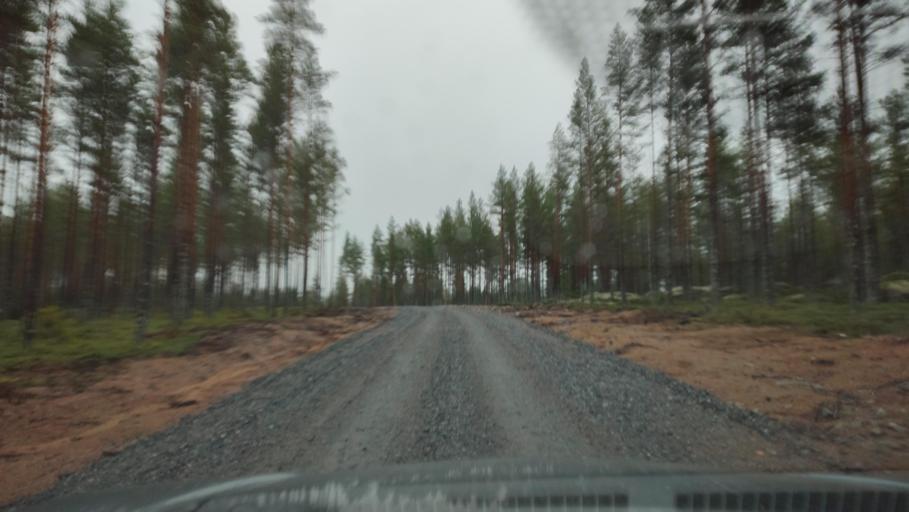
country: FI
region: Southern Ostrobothnia
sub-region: Suupohja
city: Karijoki
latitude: 62.1563
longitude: 21.6113
